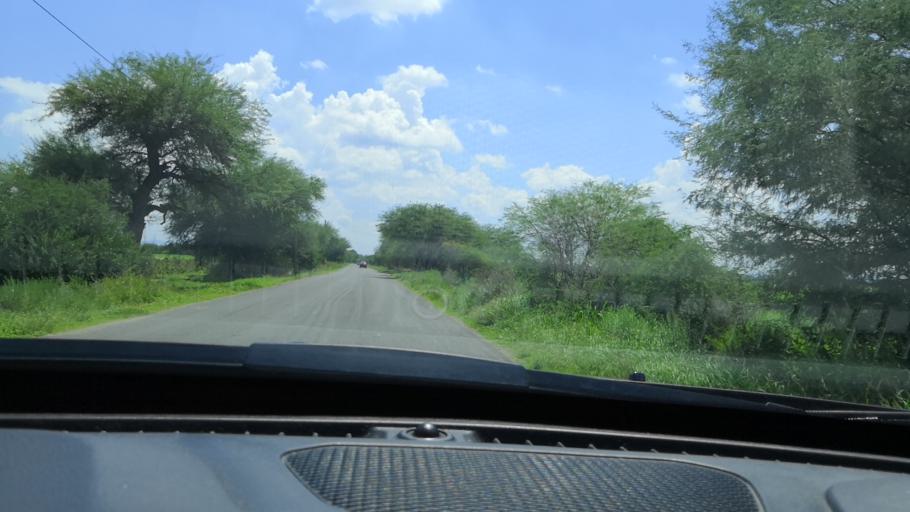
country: MX
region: Guanajuato
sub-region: Leon
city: Plan Guanajuato (La Sandia)
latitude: 20.9407
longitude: -101.6290
